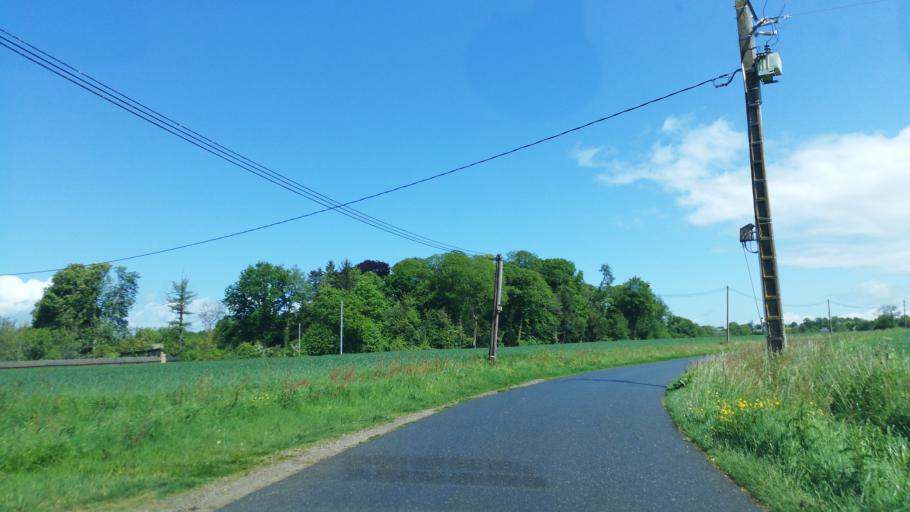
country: FR
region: Brittany
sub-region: Departement d'Ille-et-Vilaine
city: Irodouer
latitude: 48.2562
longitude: -1.9426
